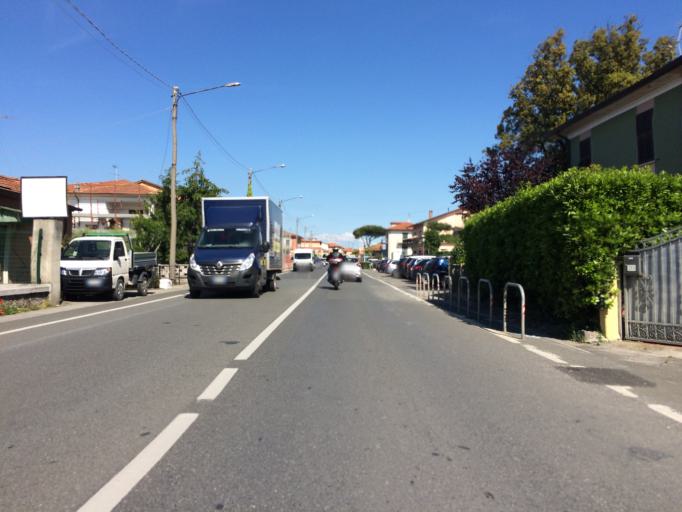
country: IT
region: Liguria
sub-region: Provincia di La Spezia
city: Casano-Dogana-Isola
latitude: 44.0677
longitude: 10.0287
